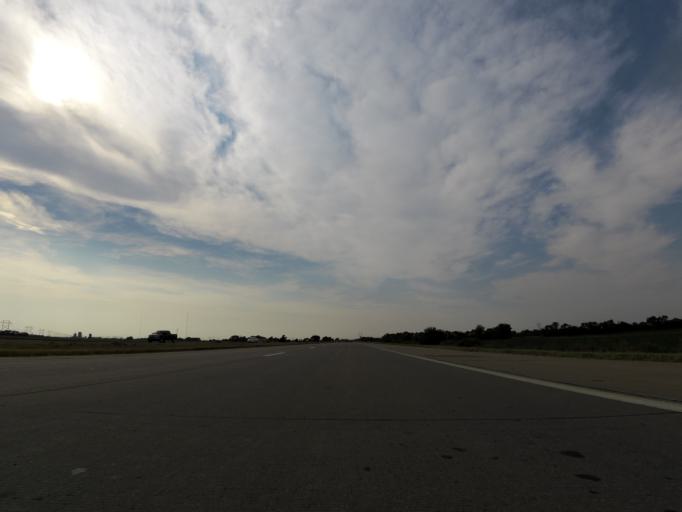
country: US
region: Kansas
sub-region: Sedgwick County
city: Maize
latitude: 37.7922
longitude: -97.4758
